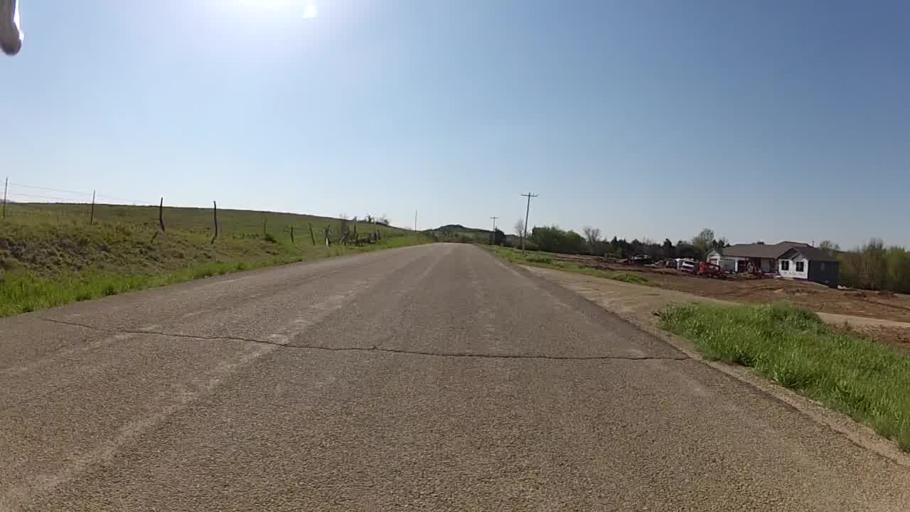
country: US
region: Kansas
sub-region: Riley County
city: Ogden
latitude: 39.0312
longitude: -96.7043
